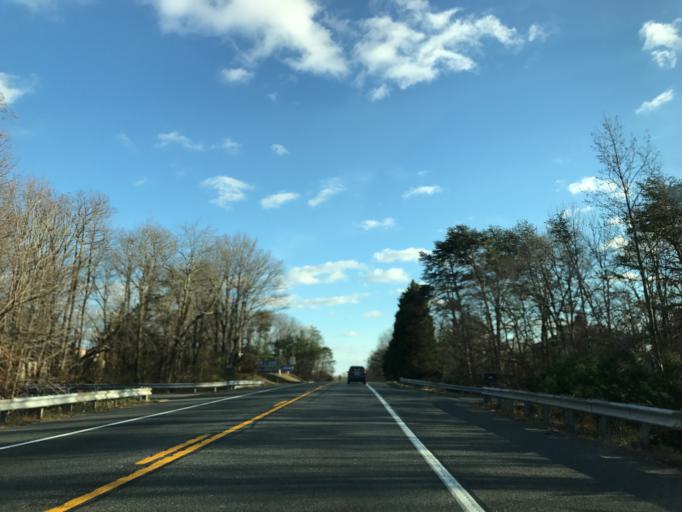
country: US
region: Maryland
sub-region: Harford County
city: Joppatowne
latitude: 39.4586
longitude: -76.3613
